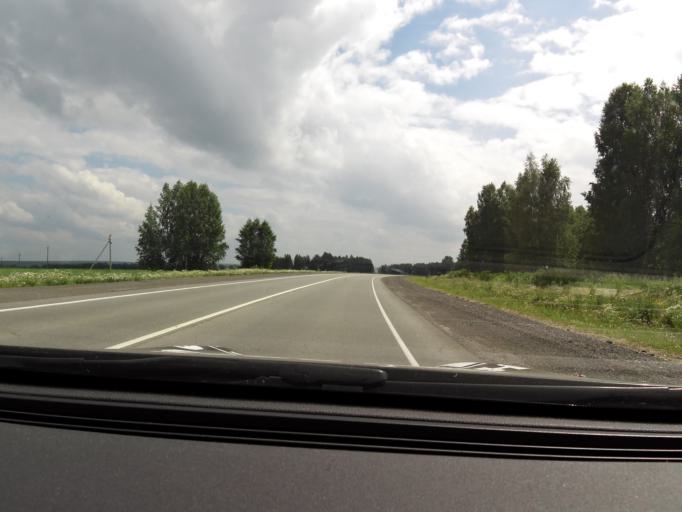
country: RU
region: Perm
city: Suksun
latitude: 56.9785
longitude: 57.5136
